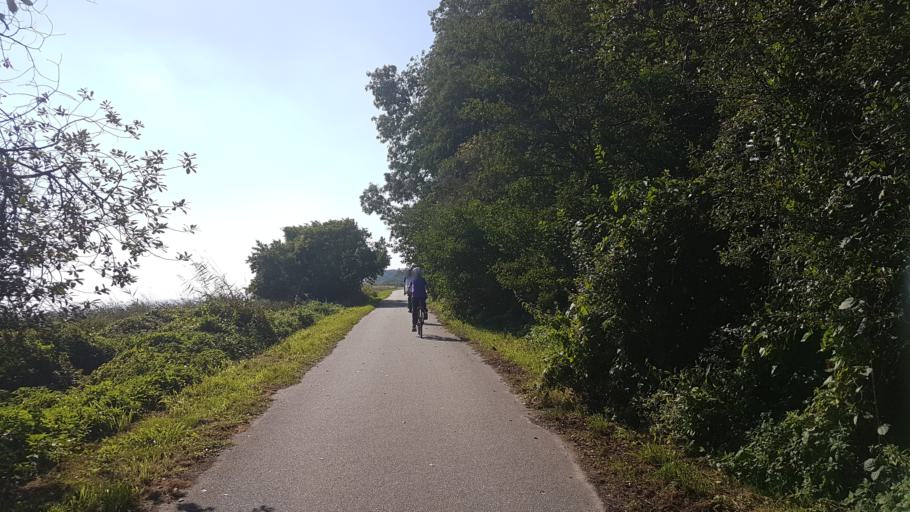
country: DE
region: Mecklenburg-Vorpommern
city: Ostseebad Binz
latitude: 54.3509
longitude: 13.5702
